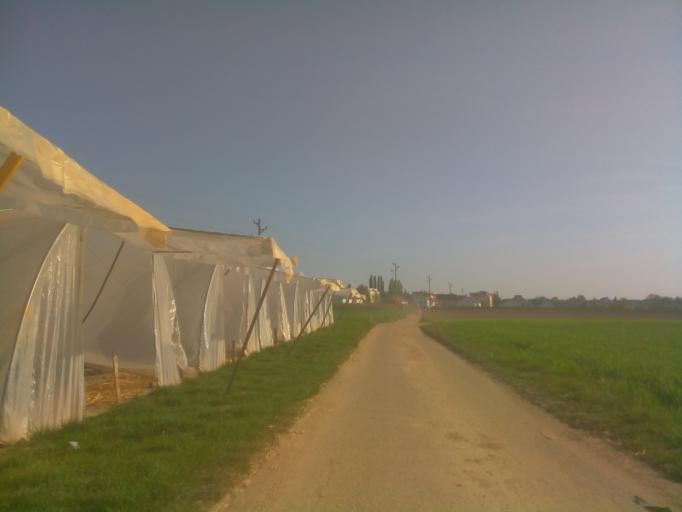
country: DE
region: Baden-Wuerttemberg
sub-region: Karlsruhe Region
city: Schriesheim
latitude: 49.5051
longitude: 8.6543
